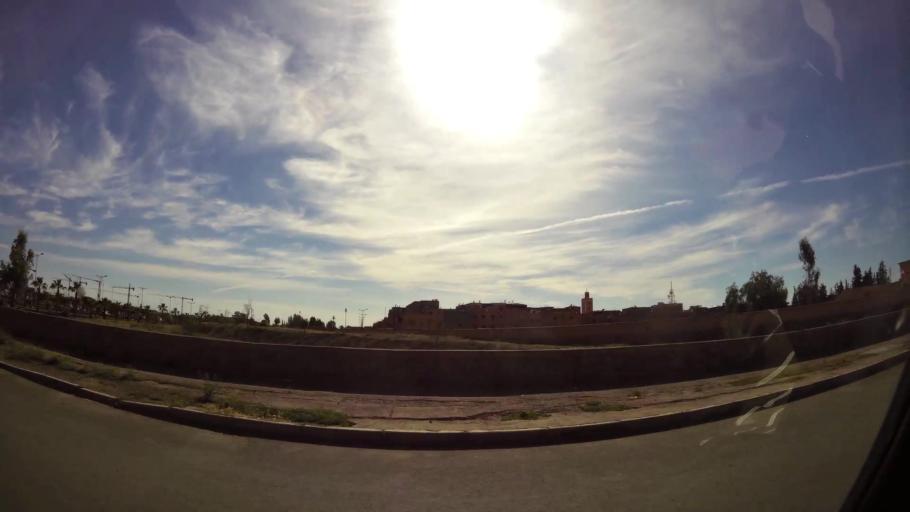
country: MA
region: Marrakech-Tensift-Al Haouz
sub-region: Marrakech
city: Marrakesh
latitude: 31.6062
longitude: -7.9568
